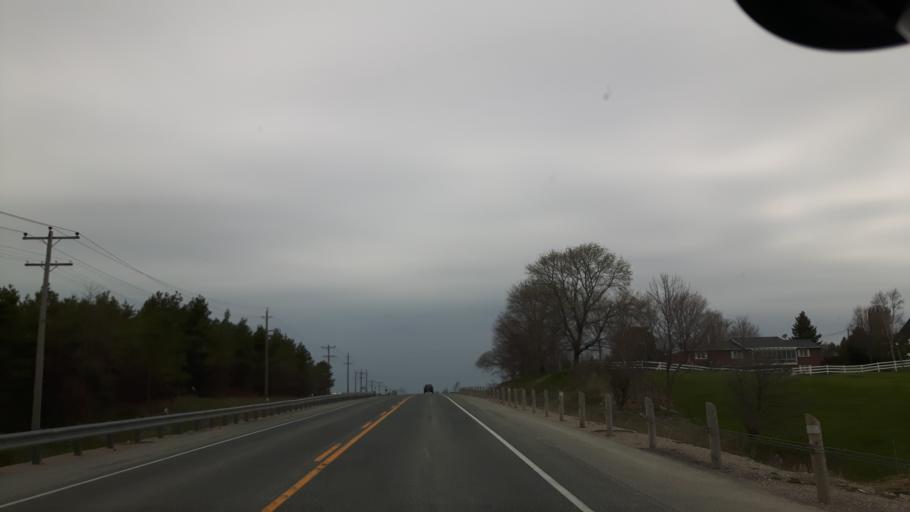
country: CA
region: Ontario
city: Goderich
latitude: 43.6715
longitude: -81.6235
